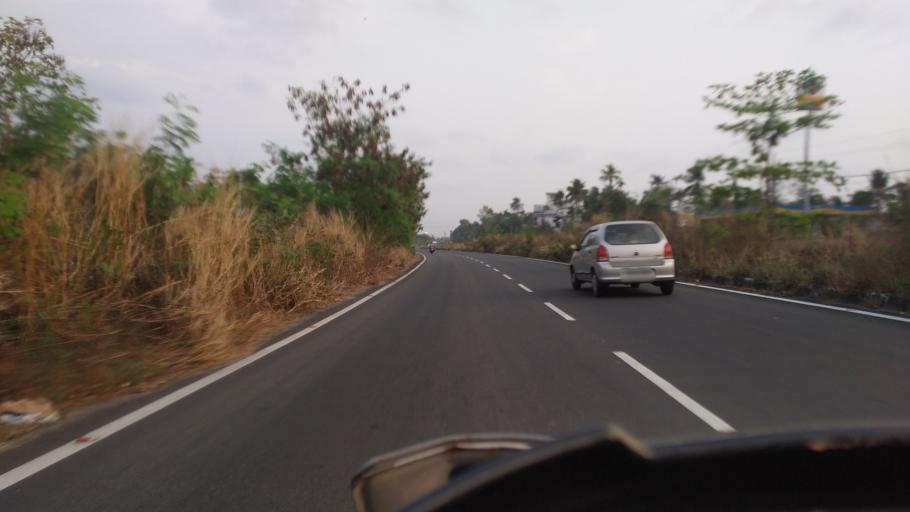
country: IN
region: Kerala
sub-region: Thrissur District
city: Kodungallur
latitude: 10.2179
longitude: 76.1965
